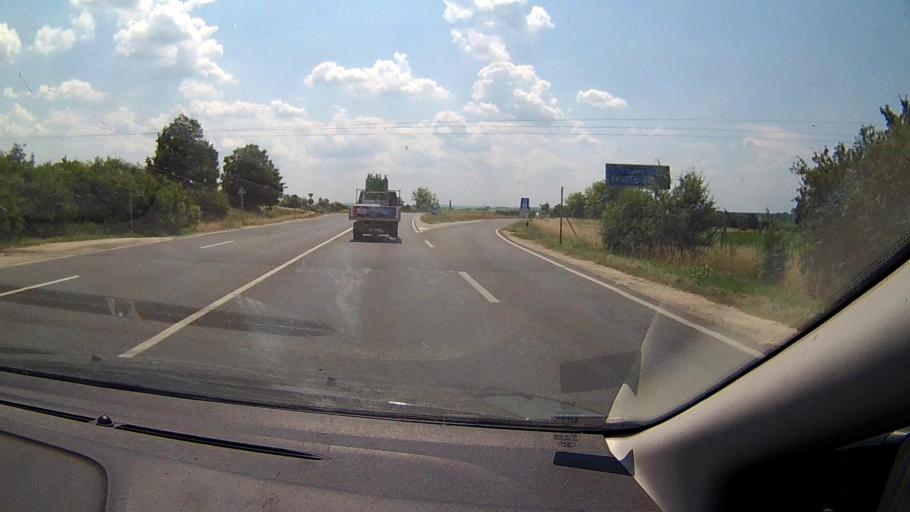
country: HU
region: Komarom-Esztergom
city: Tata
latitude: 47.6276
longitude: 18.3155
